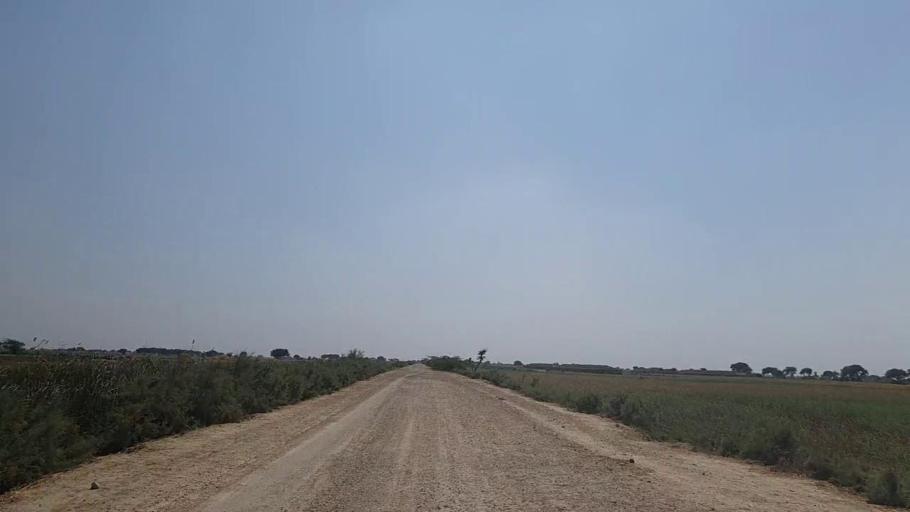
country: PK
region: Sindh
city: Mirpur Batoro
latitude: 24.5480
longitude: 68.3168
